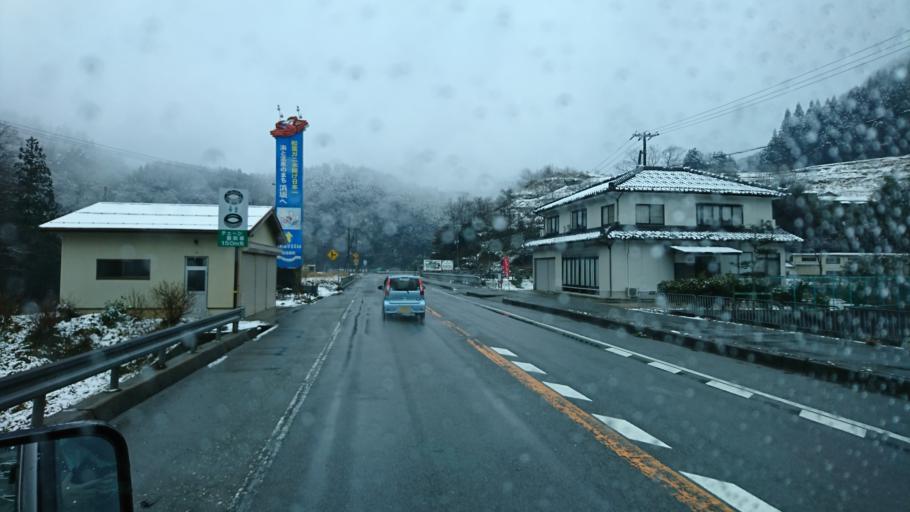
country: JP
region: Hyogo
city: Toyooka
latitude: 35.4763
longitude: 134.5864
